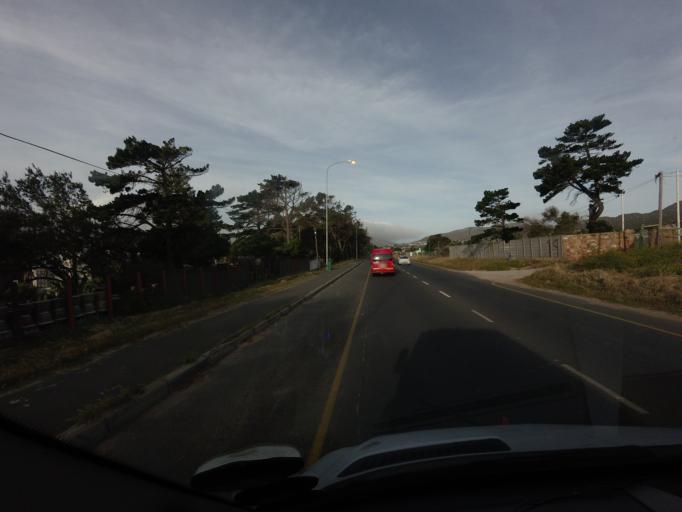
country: ZA
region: Western Cape
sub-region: City of Cape Town
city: Constantia
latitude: -34.1350
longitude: 18.3731
